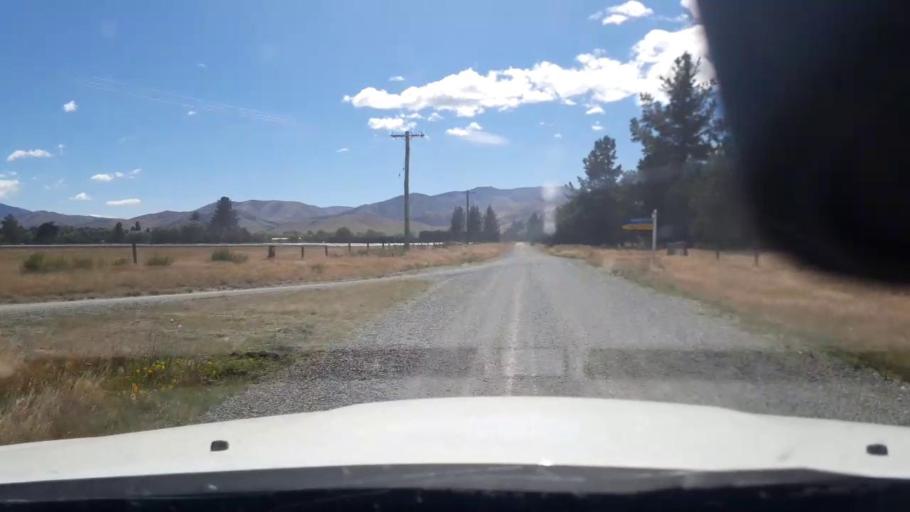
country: NZ
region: Canterbury
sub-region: Timaru District
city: Pleasant Point
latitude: -44.0022
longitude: 170.8370
